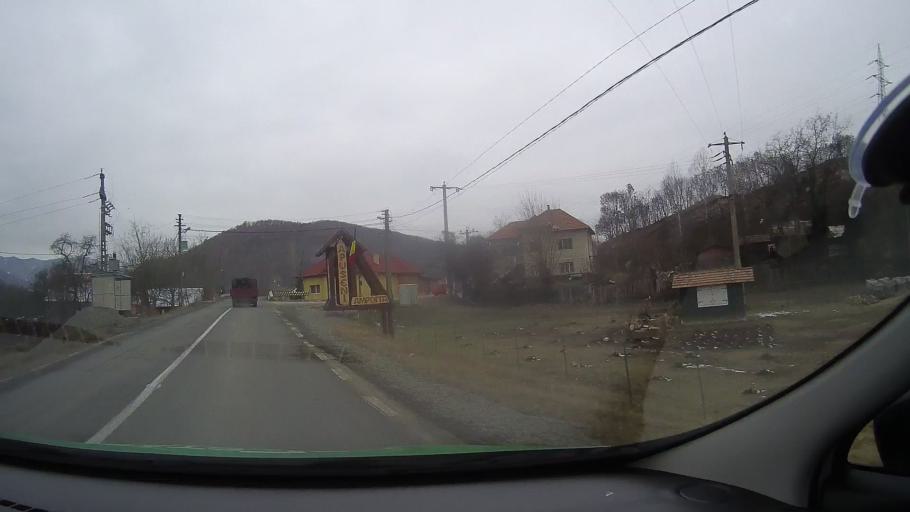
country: RO
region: Alba
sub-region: Comuna Ighiu
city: Ighiel
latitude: 46.1115
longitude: 23.4890
